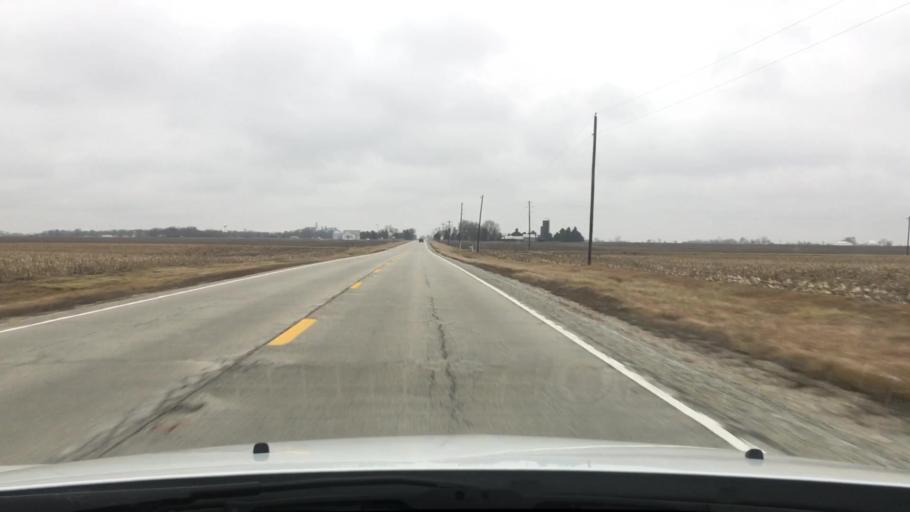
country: US
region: Illinois
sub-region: Iroquois County
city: Clifton
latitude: 40.8856
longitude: -87.9211
